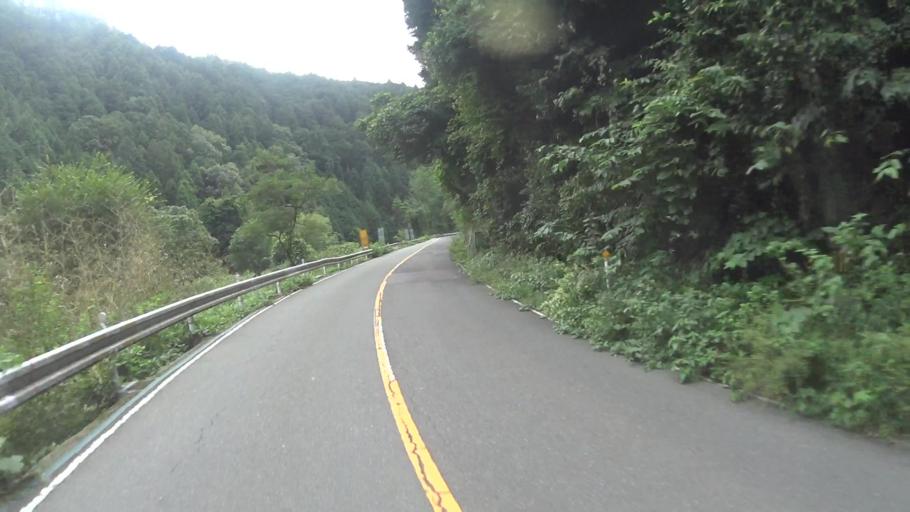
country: JP
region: Kyoto
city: Uji
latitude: 34.8148
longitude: 135.9255
